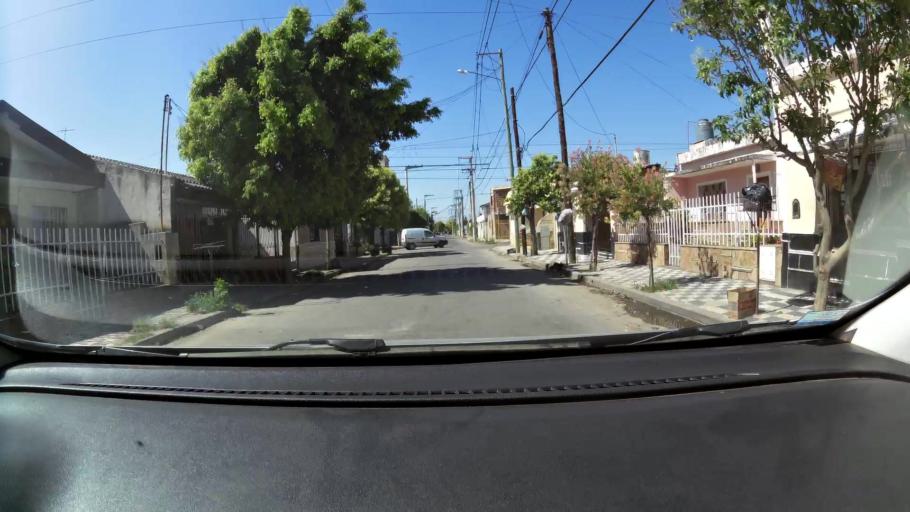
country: AR
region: Cordoba
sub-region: Departamento de Capital
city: Cordoba
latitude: -31.4377
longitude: -64.1356
